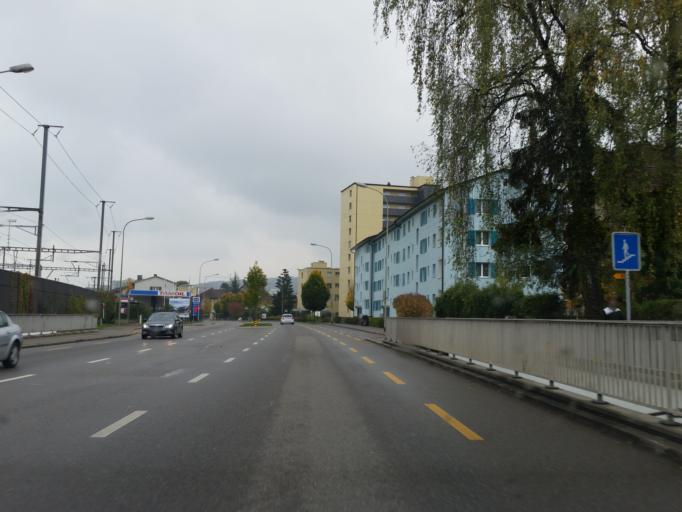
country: CH
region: Zurich
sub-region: Bezirk Dietikon
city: Dietikon / Guggenbuehl
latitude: 47.4006
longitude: 8.4097
